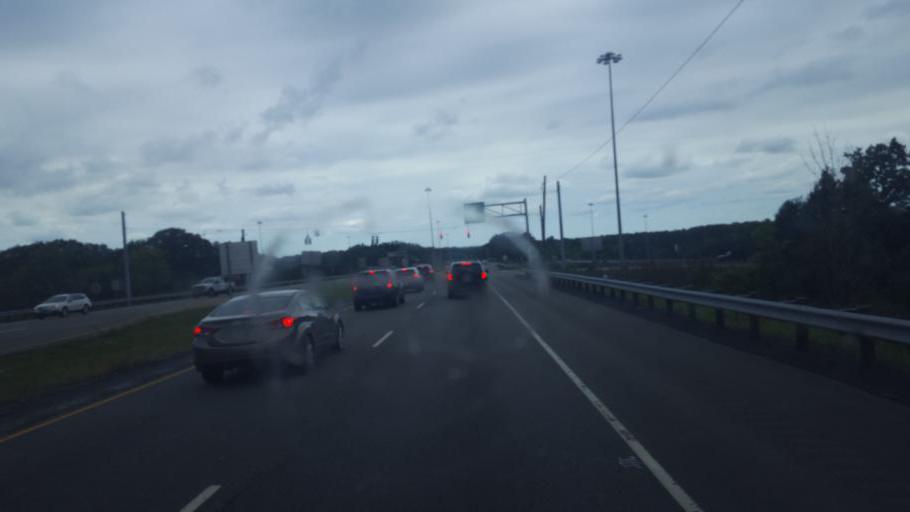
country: US
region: Ohio
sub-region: Lake County
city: Painesville
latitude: 41.6681
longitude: -81.2457
